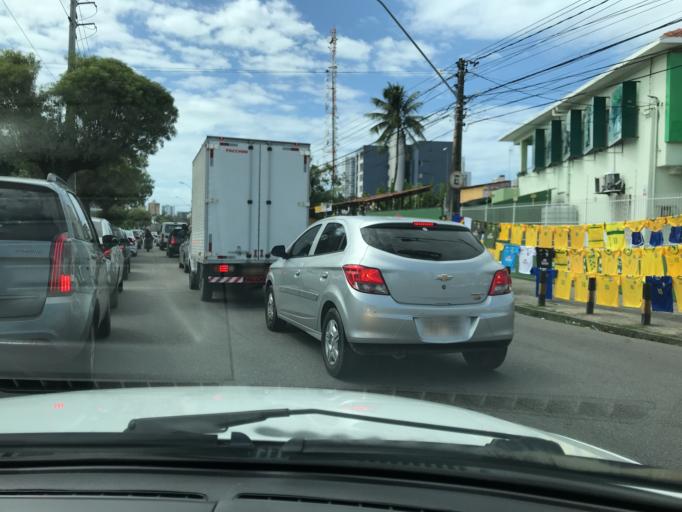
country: BR
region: Pernambuco
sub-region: Recife
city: Recife
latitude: -8.0617
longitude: -34.9076
